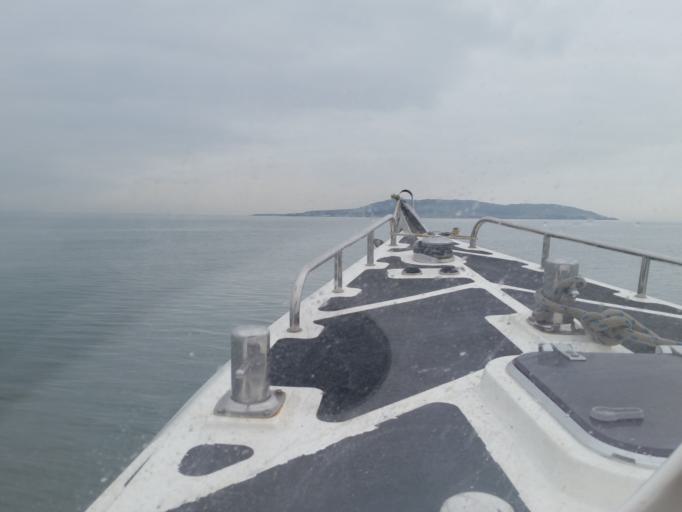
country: IE
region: Leinster
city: Portraine
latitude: 53.4719
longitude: -6.0778
